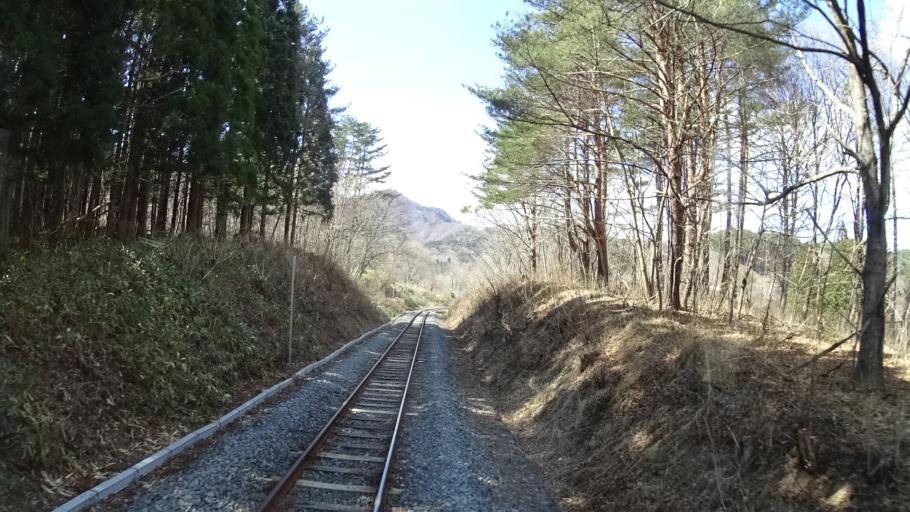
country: JP
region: Iwate
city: Yamada
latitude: 39.5091
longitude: 141.9168
